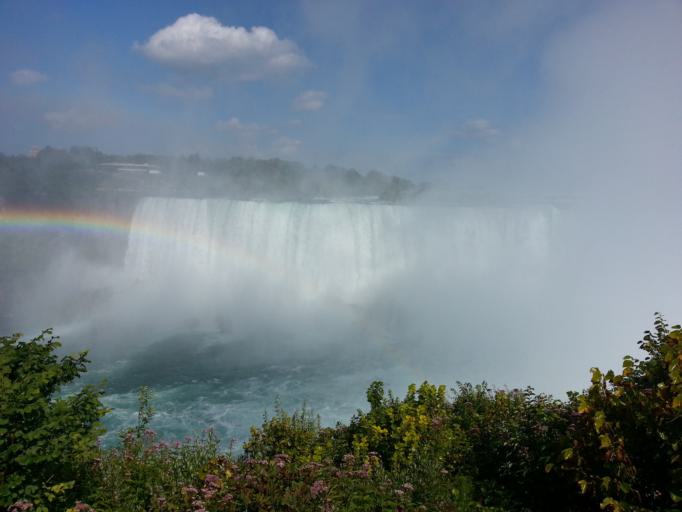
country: CA
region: Ontario
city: Niagara Falls
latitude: 43.0791
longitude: -79.0782
